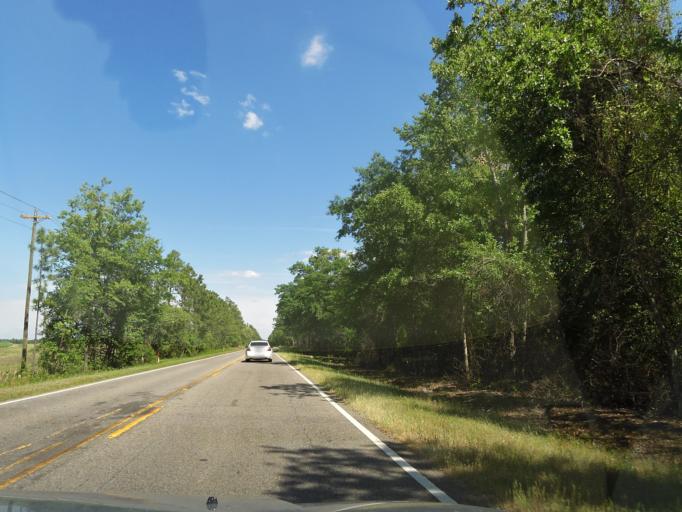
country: US
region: South Carolina
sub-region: Aiken County
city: New Ellenton
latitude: 33.5093
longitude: -81.5559
